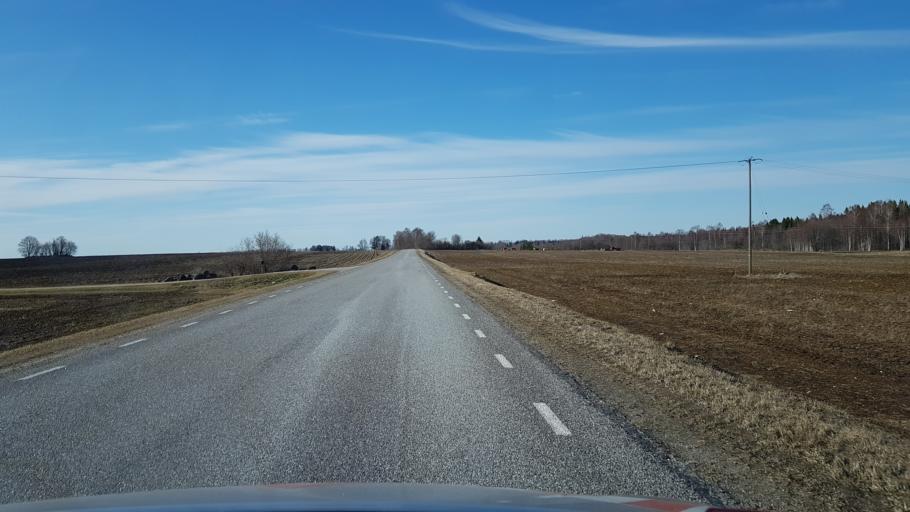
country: EE
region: Laeaene-Virumaa
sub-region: Kadrina vald
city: Kadrina
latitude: 59.3194
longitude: 26.1462
